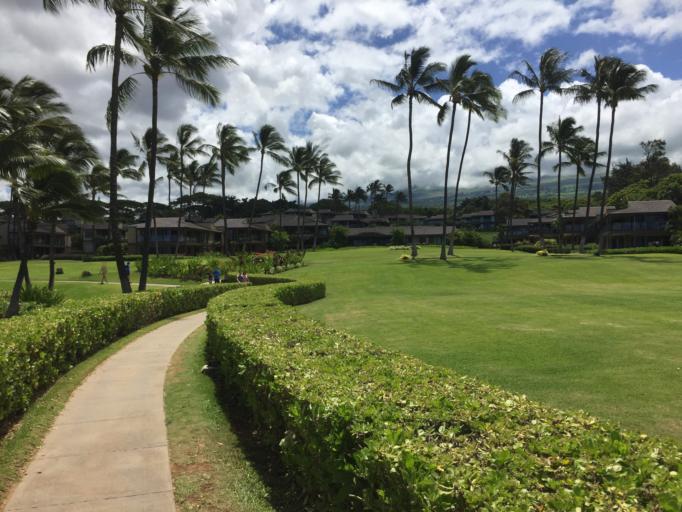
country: US
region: Hawaii
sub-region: Maui County
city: Kihei
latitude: 20.6892
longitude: -156.4438
